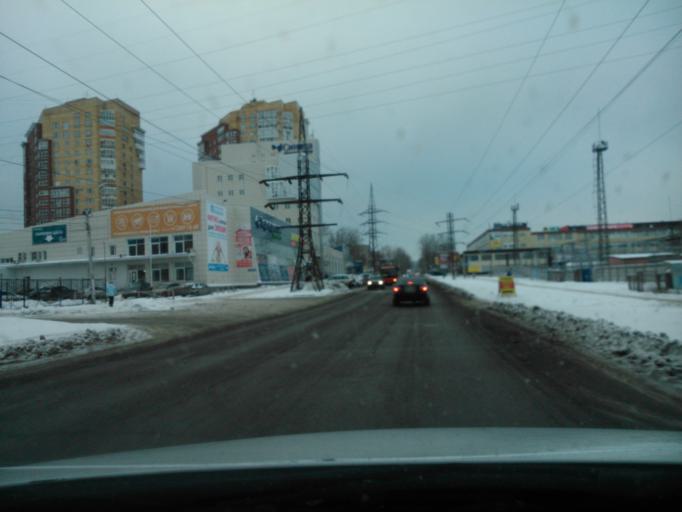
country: RU
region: Perm
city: Perm
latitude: 57.9872
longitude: 56.2107
